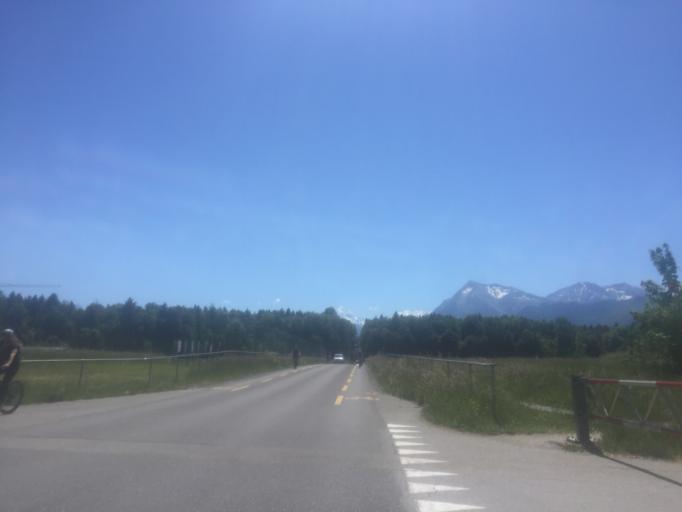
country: CH
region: Bern
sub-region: Thun District
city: Thierachern
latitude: 46.7488
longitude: 7.5902
